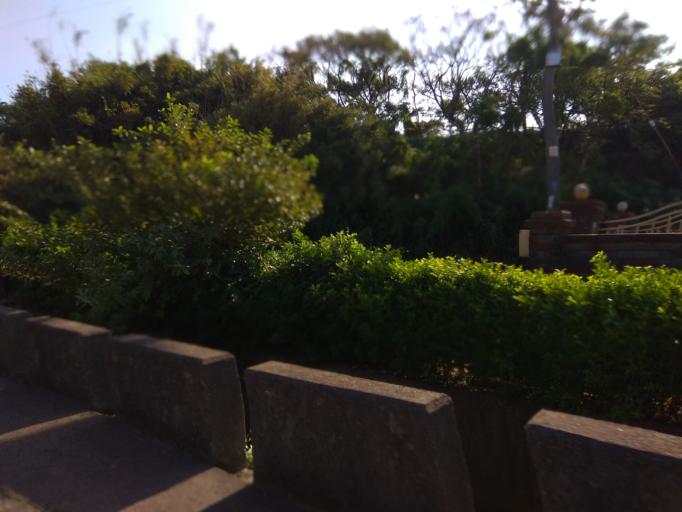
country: TW
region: Taiwan
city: Taoyuan City
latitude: 25.0622
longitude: 121.2158
